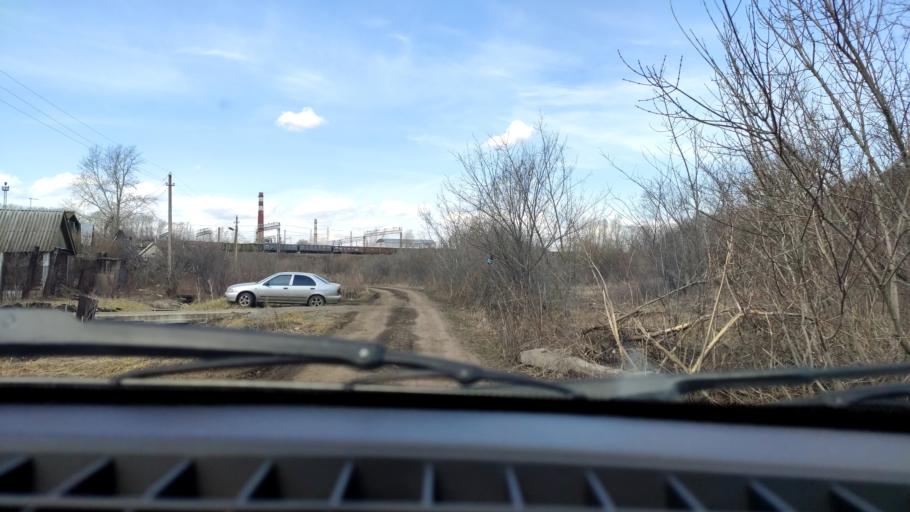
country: RU
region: Bashkortostan
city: Avdon
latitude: 54.6809
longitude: 55.8207
